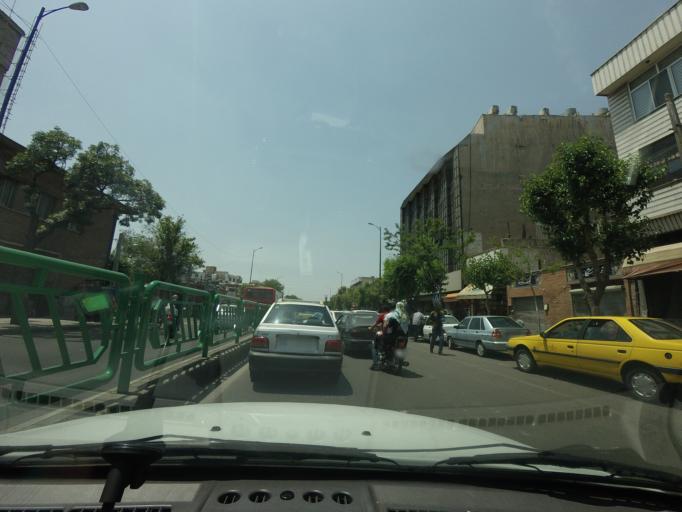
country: IR
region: Tehran
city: Tehran
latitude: 35.6690
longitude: 51.4262
